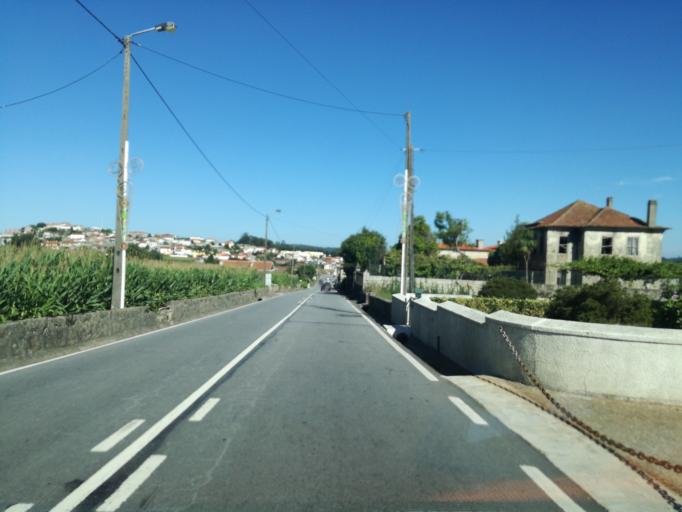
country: PT
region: Porto
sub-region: Trofa
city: Sao Romao do Coronado
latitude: 41.2837
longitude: -8.5728
